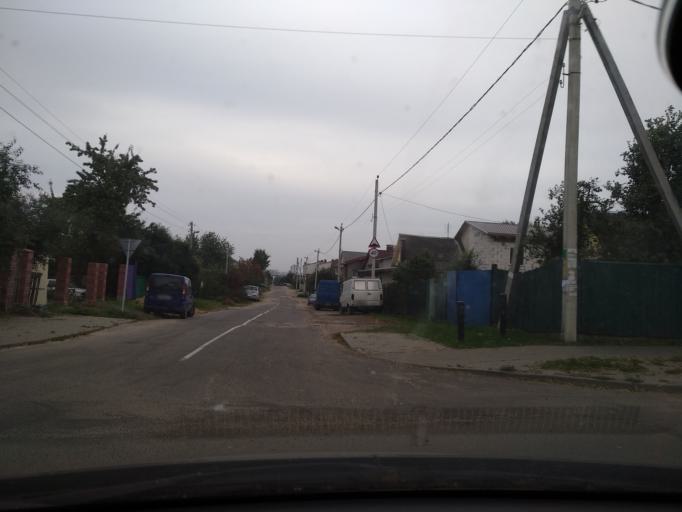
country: BY
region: Minsk
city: Minsk
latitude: 53.9441
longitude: 27.5862
